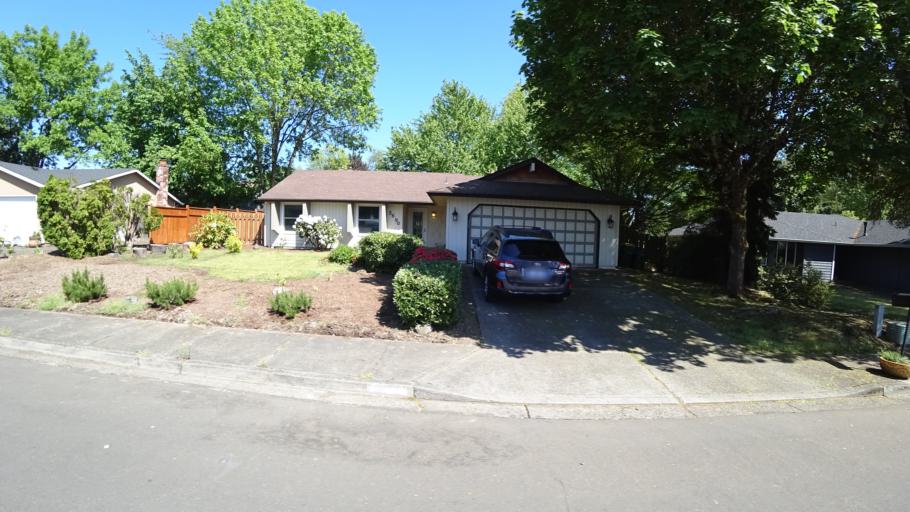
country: US
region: Oregon
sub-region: Washington County
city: Aloha
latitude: 45.4787
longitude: -122.8449
